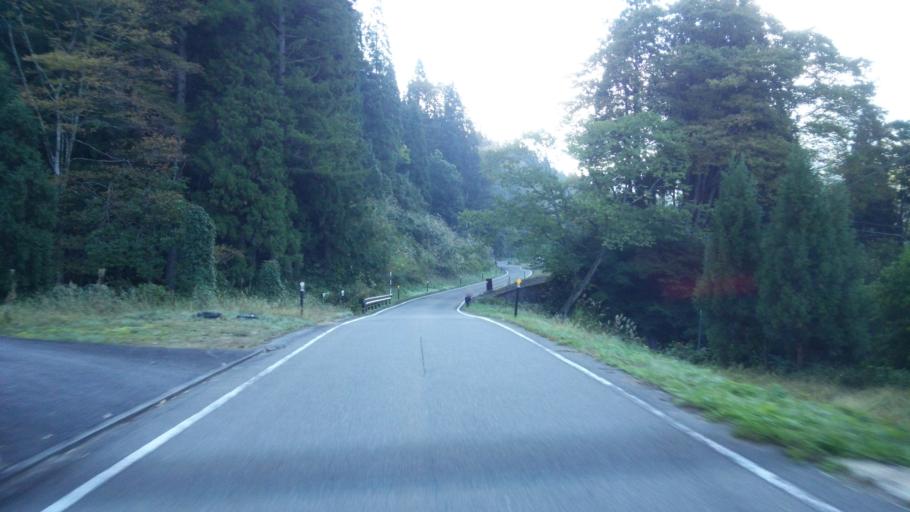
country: JP
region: Fukushima
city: Kitakata
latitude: 37.4170
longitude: 139.7297
